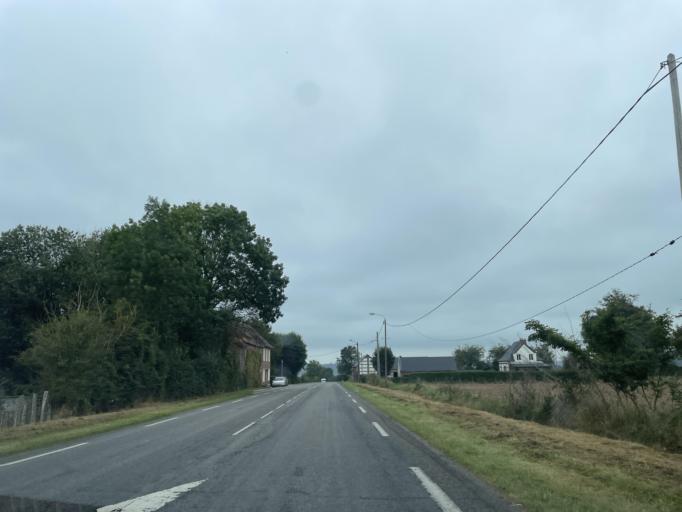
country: FR
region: Haute-Normandie
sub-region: Departement de la Seine-Maritime
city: Eu
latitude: 50.0359
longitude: 1.4079
